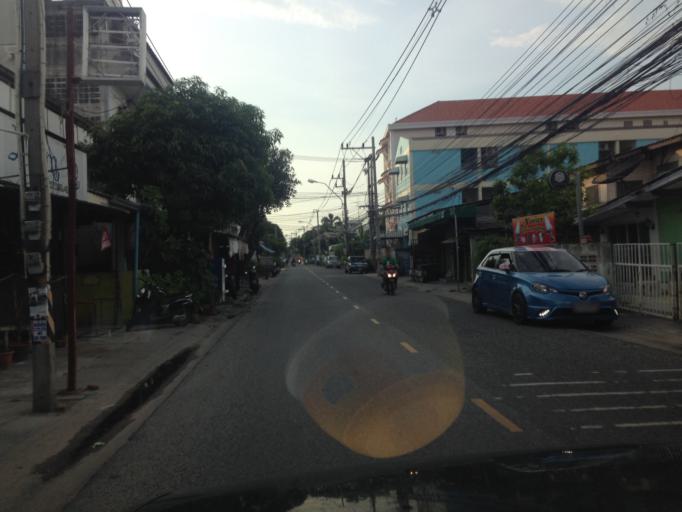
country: TH
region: Chon Buri
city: Si Racha
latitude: 13.2778
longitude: 100.9215
